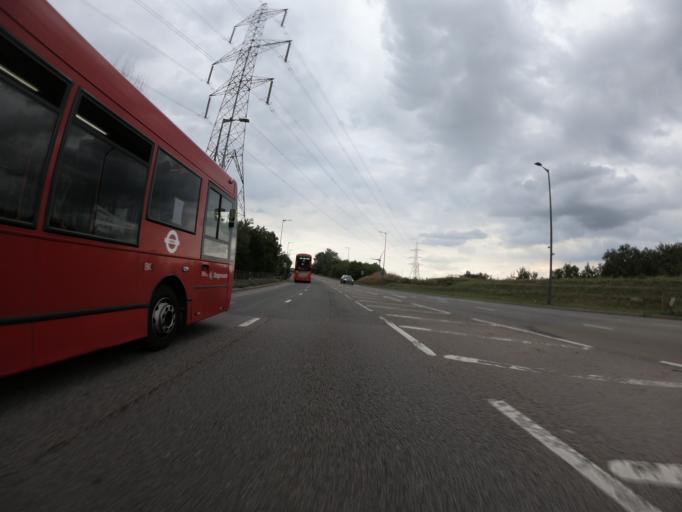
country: GB
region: England
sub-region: Greater London
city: Barking
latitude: 51.5159
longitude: 0.0720
